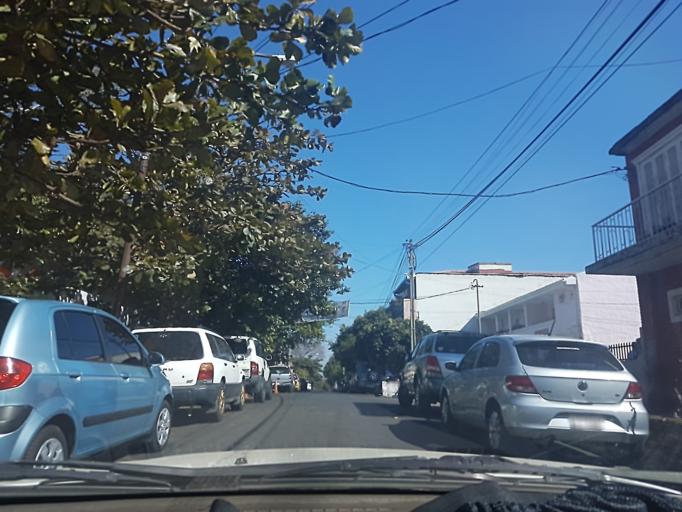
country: PY
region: Presidente Hayes
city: Nanawa
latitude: -25.2856
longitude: -57.6550
